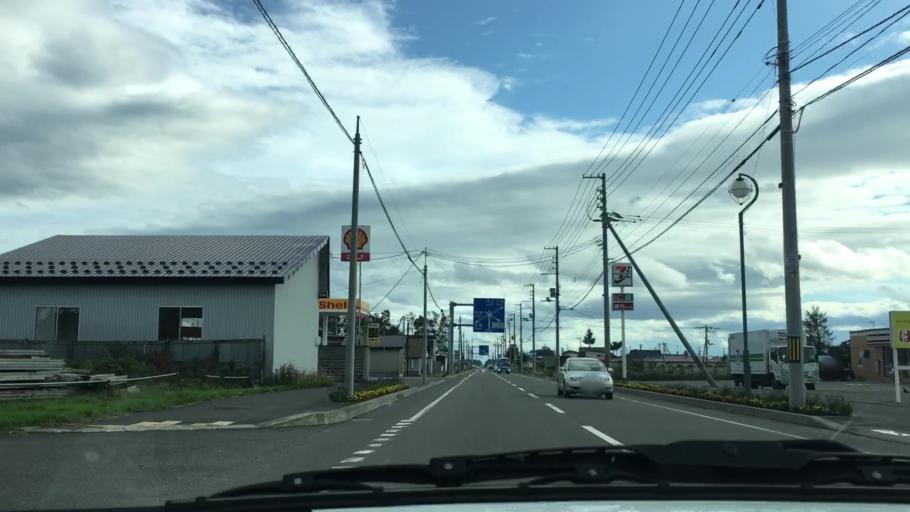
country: JP
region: Hokkaido
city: Otofuke
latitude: 43.2289
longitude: 143.2942
